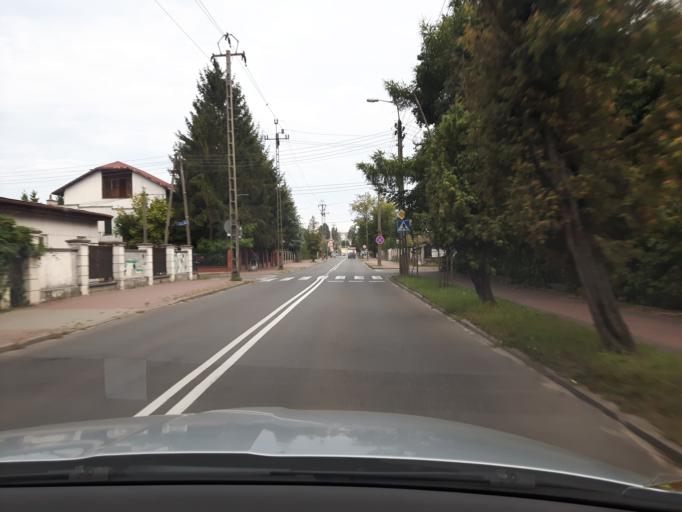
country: PL
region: Masovian Voivodeship
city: Zielonka
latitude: 52.3059
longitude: 21.1578
